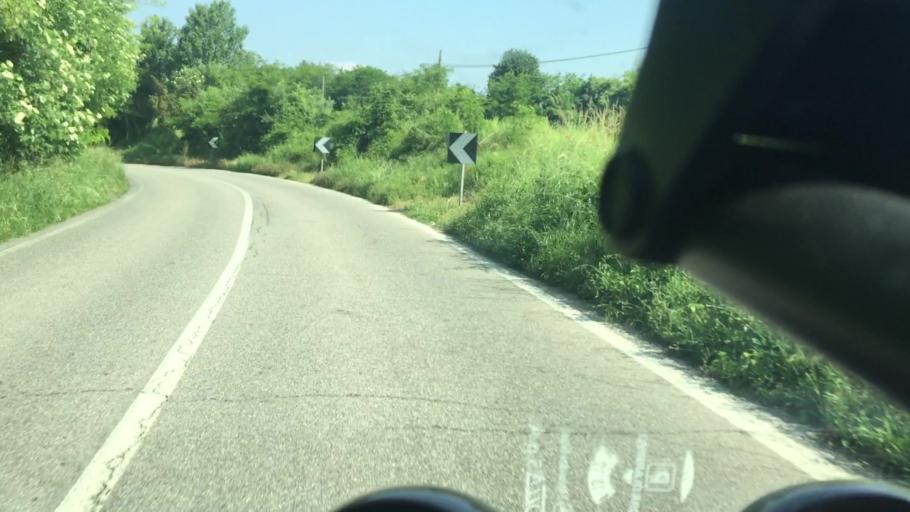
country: IT
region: Lombardy
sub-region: Provincia di Bergamo
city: Pontirolo Nuovo
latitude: 45.5542
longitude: 9.5661
